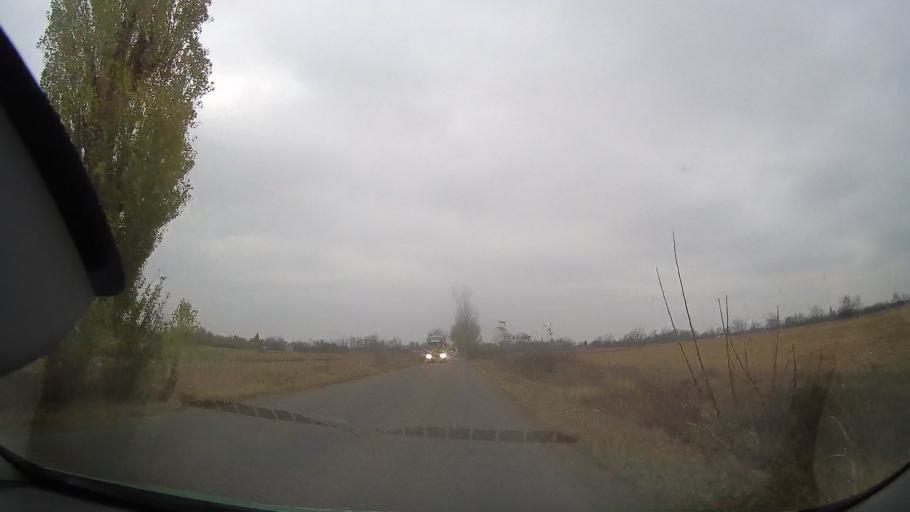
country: RO
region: Buzau
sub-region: Comuna Glodeanu-Silistea
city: Glodeanu-Silistea
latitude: 44.8245
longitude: 26.8374
